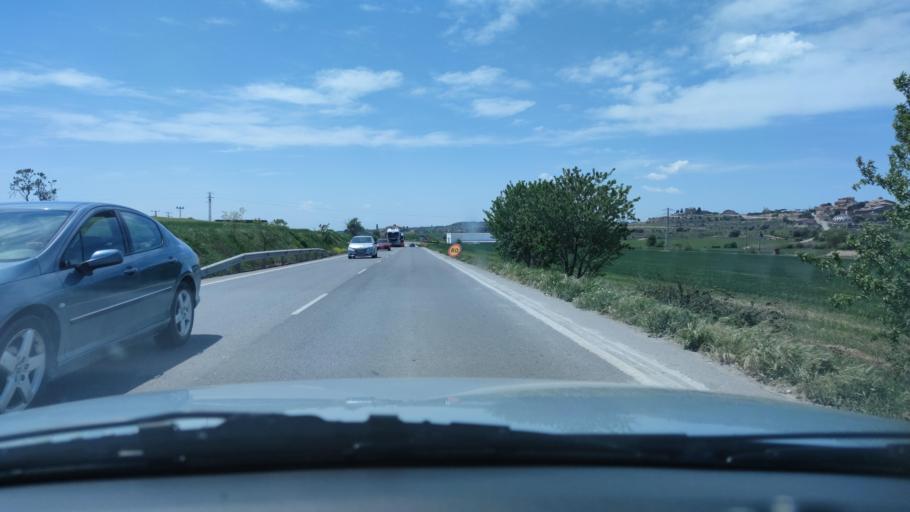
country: ES
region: Catalonia
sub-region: Provincia de Lleida
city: Mont-roig del Camp
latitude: 41.7796
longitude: 1.2745
